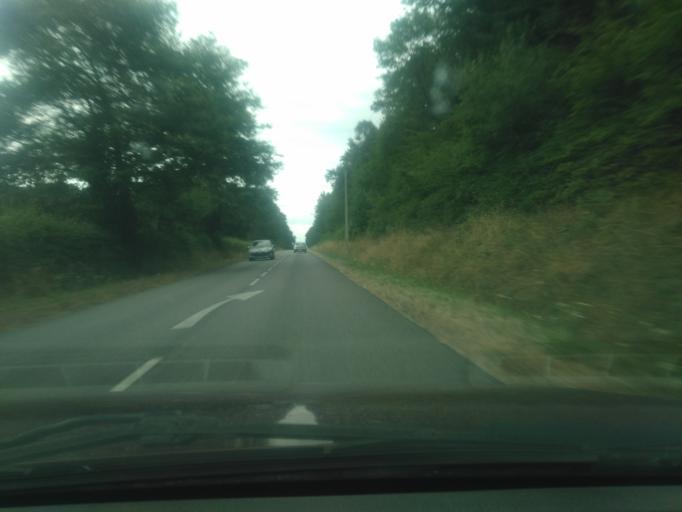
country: FR
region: Bourgogne
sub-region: Departement de la Nievre
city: Dornes
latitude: 46.7716
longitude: 3.3258
